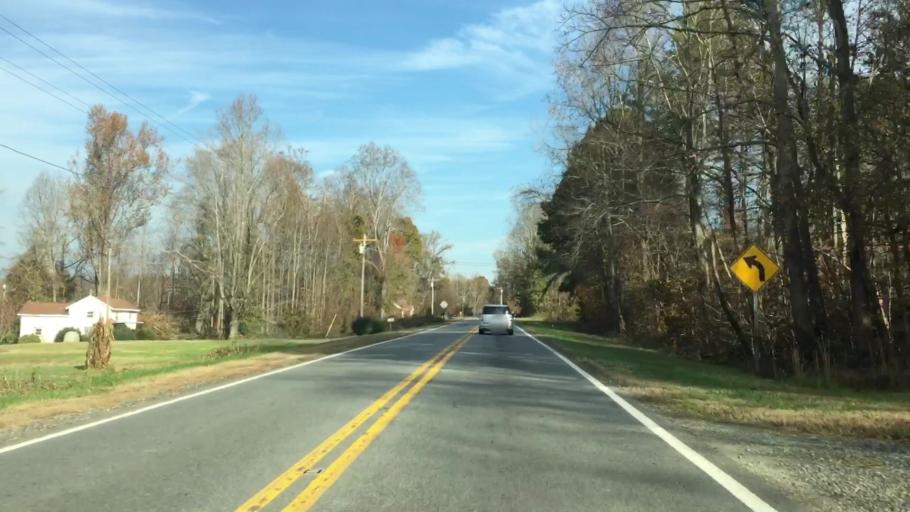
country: US
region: North Carolina
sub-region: Guilford County
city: Stokesdale
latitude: 36.2320
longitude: -80.0178
